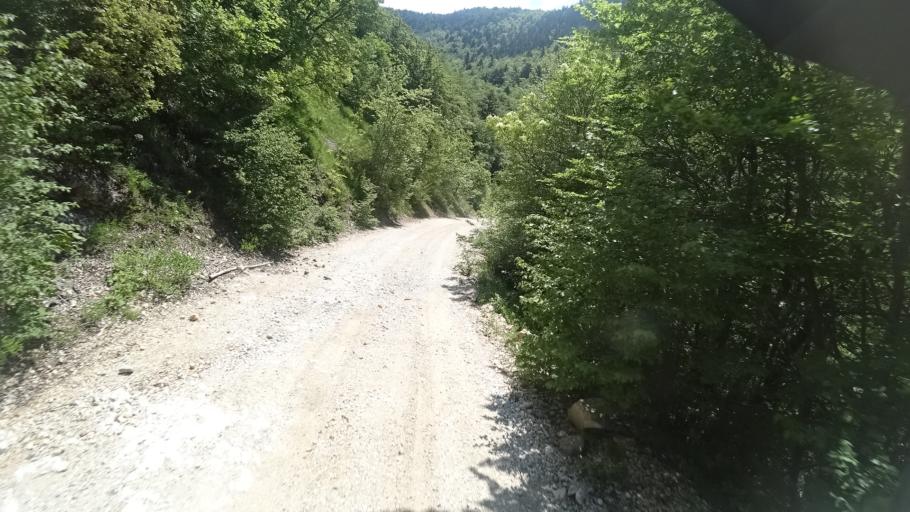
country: BA
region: Federation of Bosnia and Herzegovina
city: Orasac
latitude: 44.5731
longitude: 15.8577
